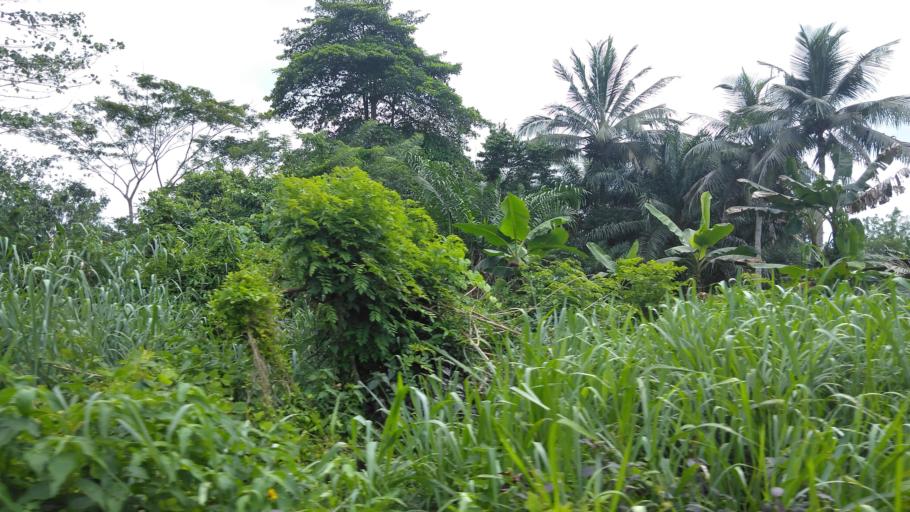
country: NG
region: Ogun
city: Abigi
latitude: 6.5957
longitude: 4.4961
